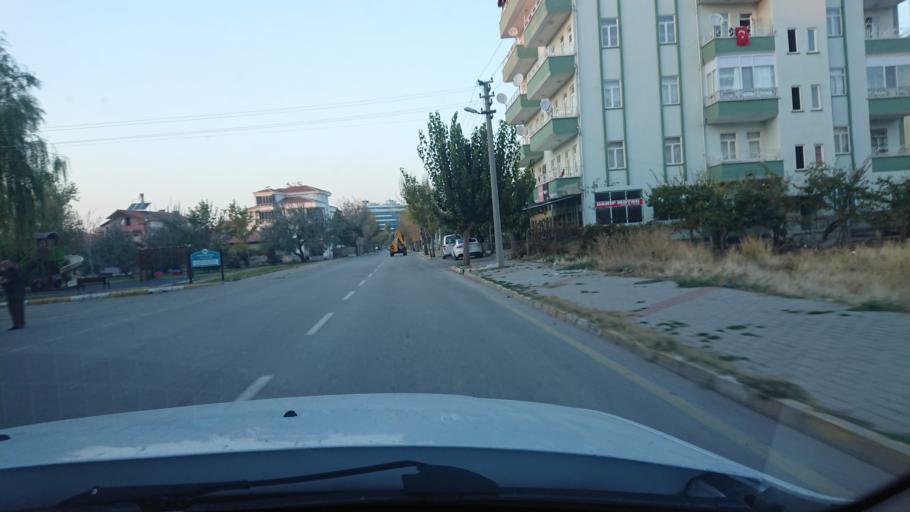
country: TR
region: Aksaray
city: Aksaray
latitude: 38.3544
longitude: 34.0421
